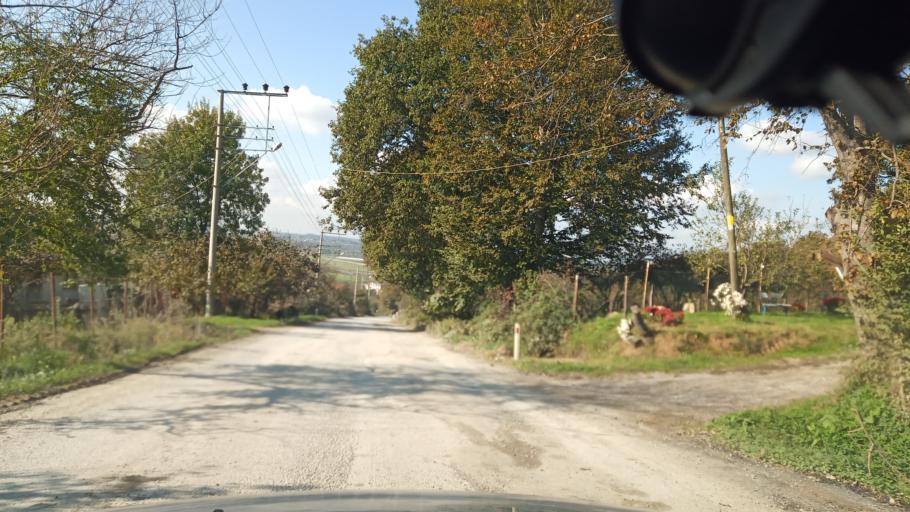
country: TR
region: Sakarya
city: Ferizli
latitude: 41.0914
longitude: 30.4514
